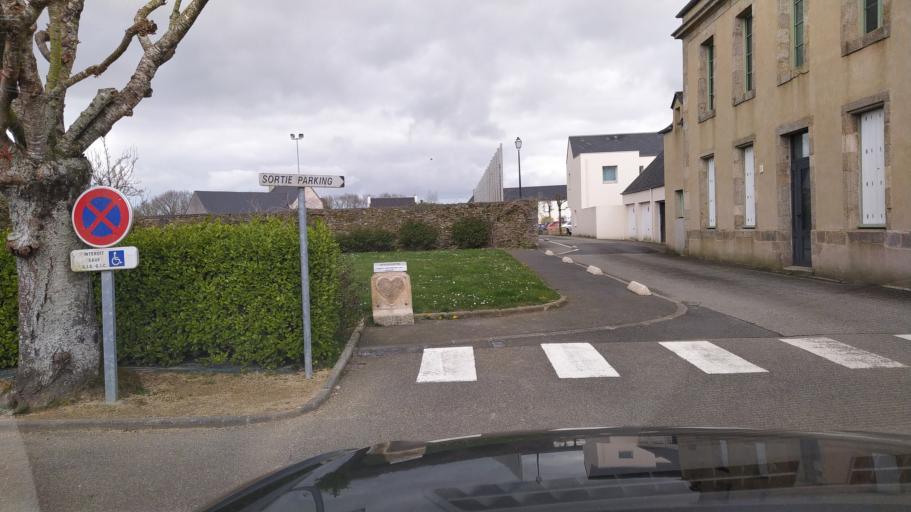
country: FR
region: Brittany
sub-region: Departement du Finistere
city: Bodilis
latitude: 48.5304
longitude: -4.1172
